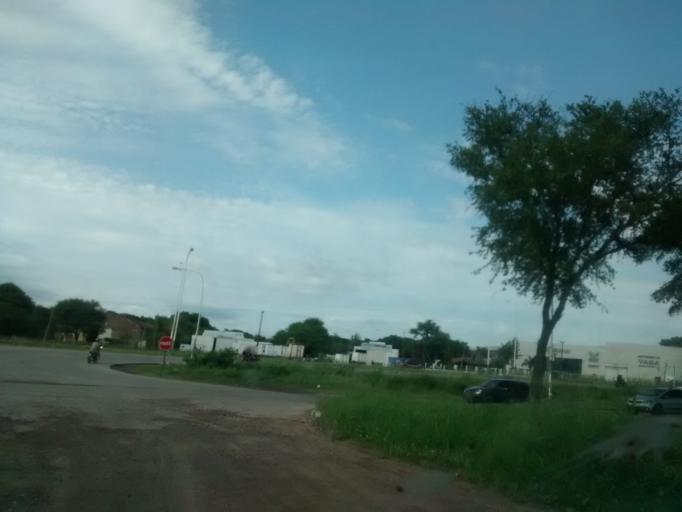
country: AR
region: Chaco
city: Resistencia
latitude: -27.4161
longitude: -58.9649
